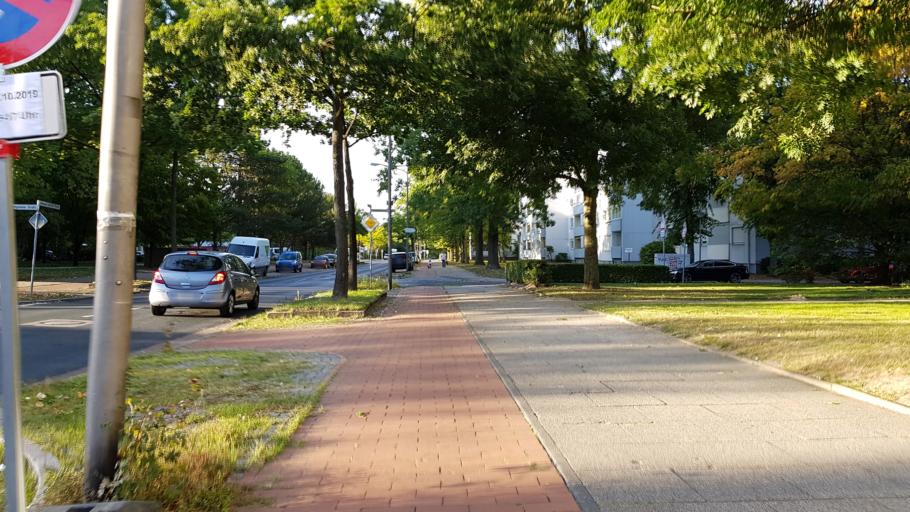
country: DE
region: Lower Saxony
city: Riede
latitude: 53.0396
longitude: 8.9324
